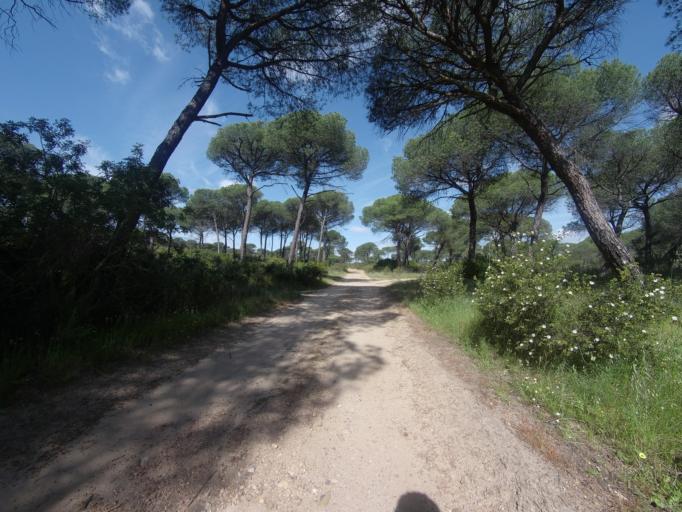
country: ES
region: Andalusia
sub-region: Provincia de Huelva
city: Aljaraque
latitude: 37.2359
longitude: -7.0551
